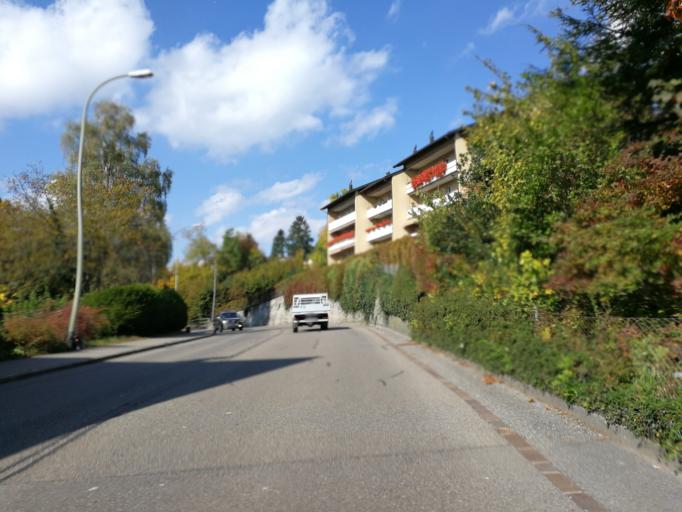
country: CH
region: Zurich
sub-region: Bezirk Meilen
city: Mannedorf
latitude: 47.2592
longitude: 8.6991
